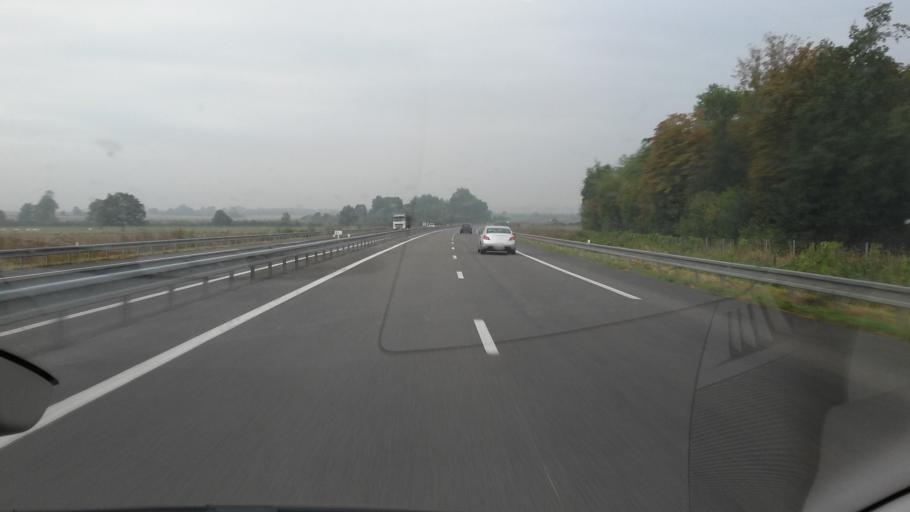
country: FR
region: Champagne-Ardenne
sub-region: Departement des Ardennes
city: Rethel
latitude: 49.5624
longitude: 4.4660
